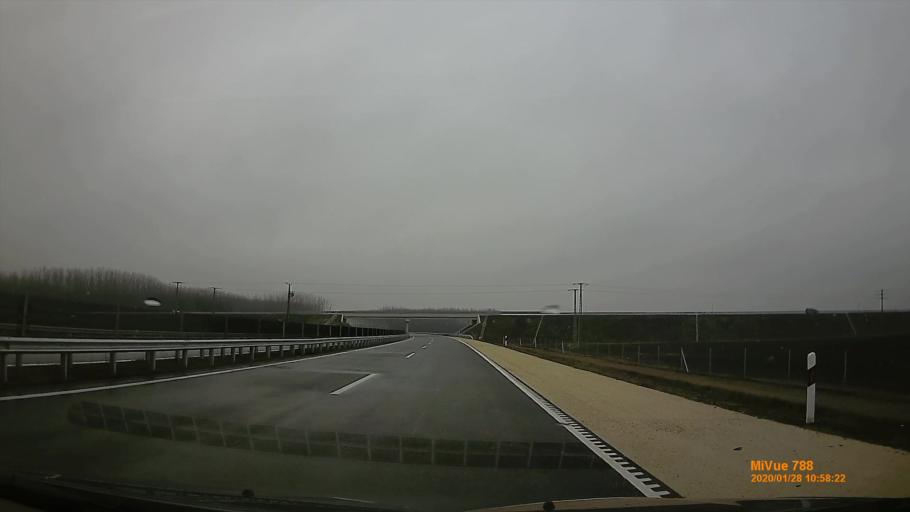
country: HU
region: Pest
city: Peteri
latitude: 47.3769
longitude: 19.4013
